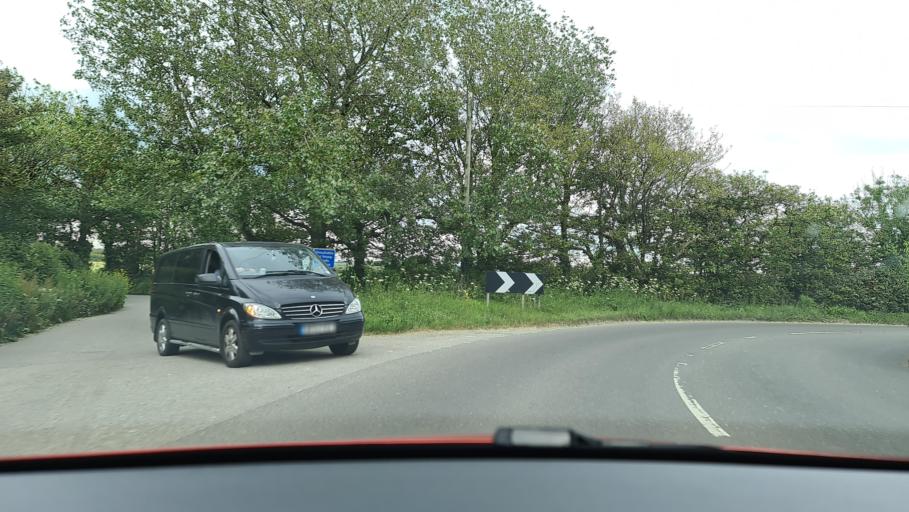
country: GB
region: England
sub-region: Cornwall
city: Bude
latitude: 50.8177
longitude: -4.5305
